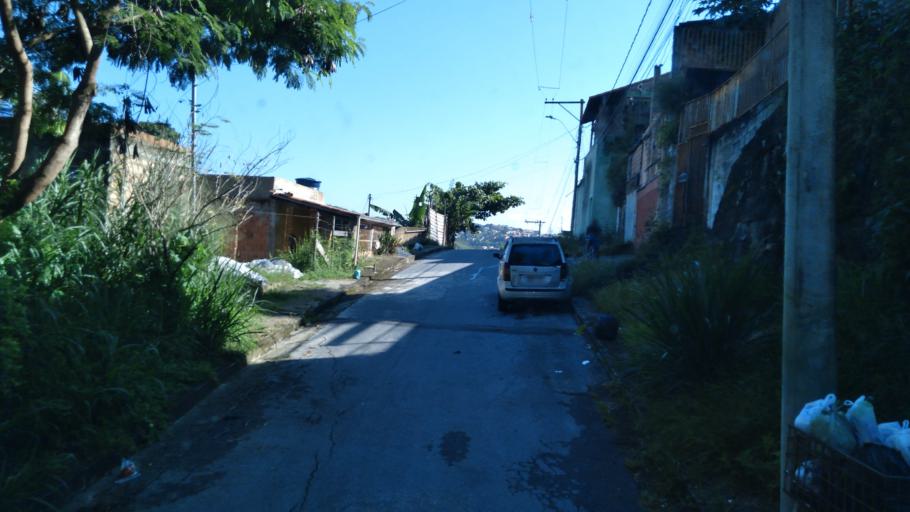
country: BR
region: Minas Gerais
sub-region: Santa Luzia
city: Santa Luzia
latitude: -19.8281
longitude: -43.8985
